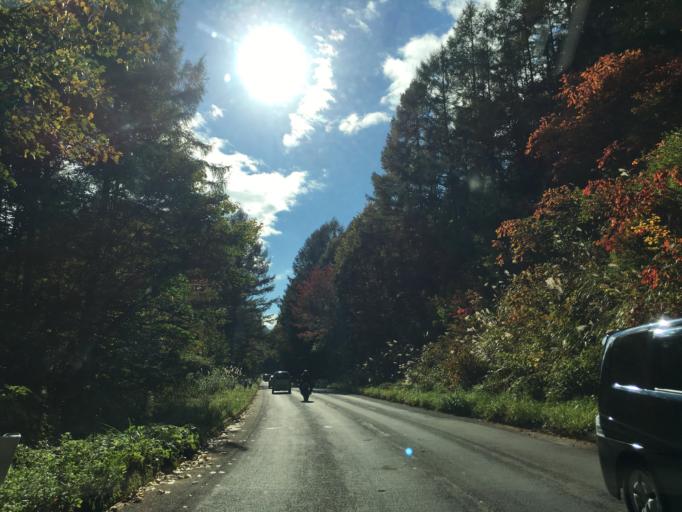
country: JP
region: Fukushima
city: Inawashiro
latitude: 37.6614
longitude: 140.1484
